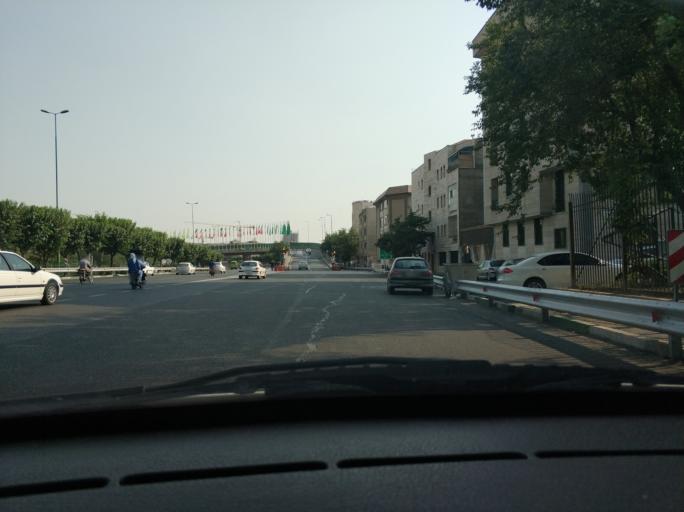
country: IR
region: Tehran
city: Tehran
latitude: 35.7381
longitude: 51.4587
